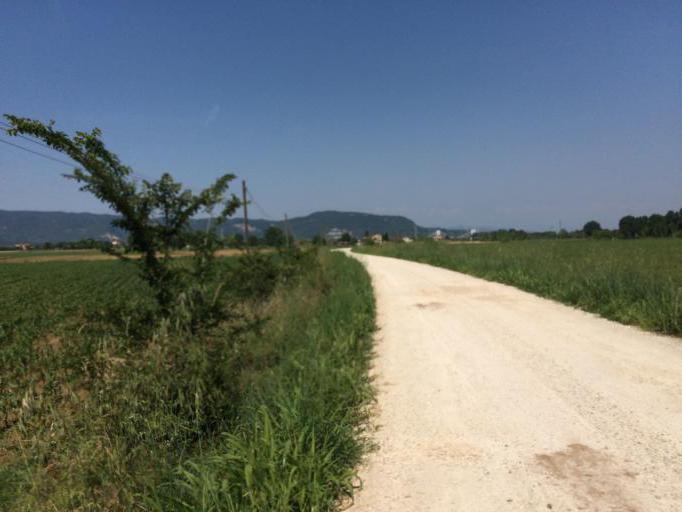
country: IT
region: Veneto
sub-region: Provincia di Vicenza
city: Montegaldella
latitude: 45.4480
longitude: 11.6547
